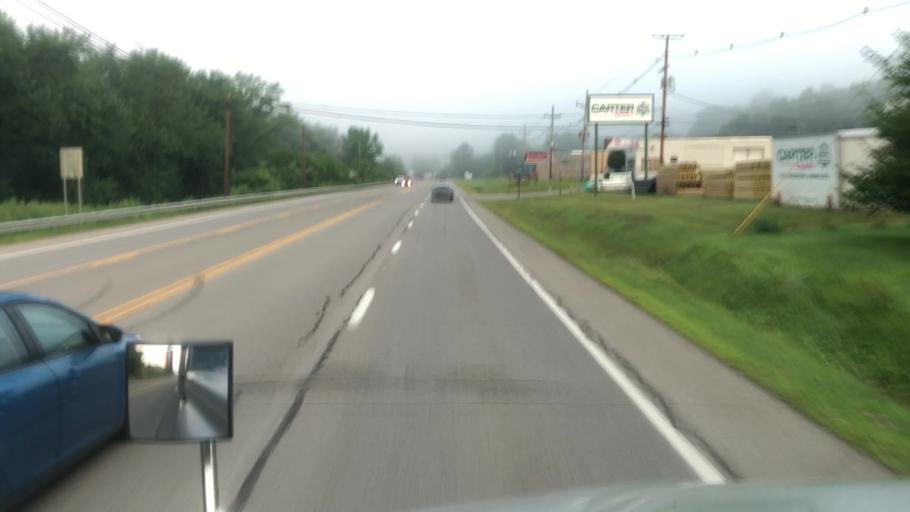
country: US
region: Pennsylvania
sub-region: Venango County
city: Woodland Heights
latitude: 41.4153
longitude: -79.7656
